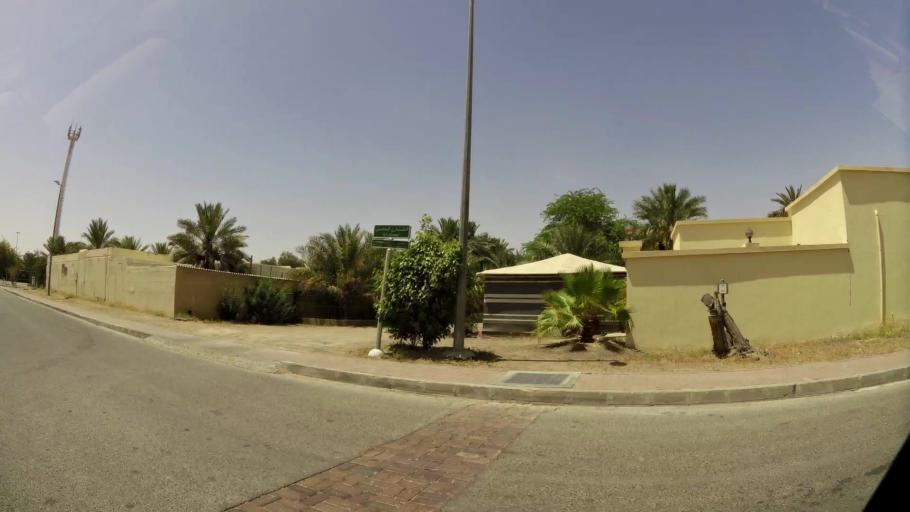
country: OM
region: Al Buraimi
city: Al Buraymi
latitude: 24.2863
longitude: 55.7653
